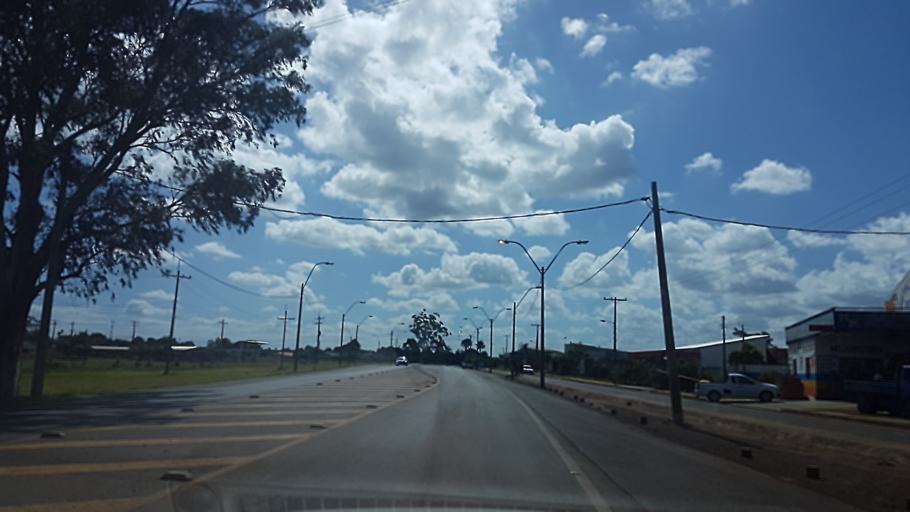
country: PY
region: Itapua
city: Carmen del Parana
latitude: -27.2196
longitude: -56.1396
